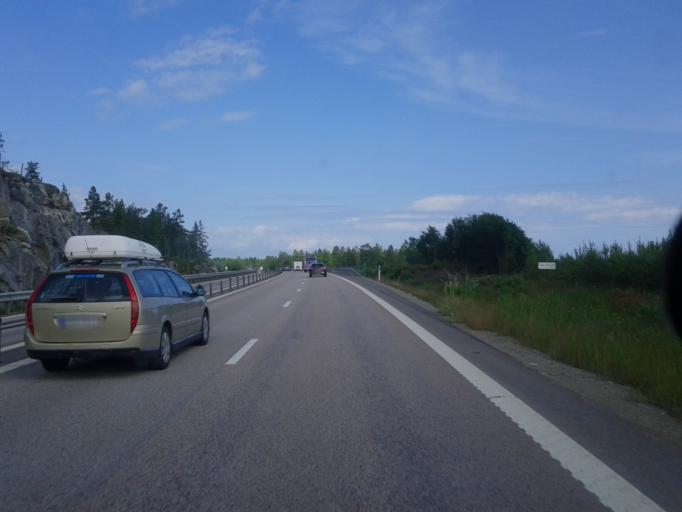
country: SE
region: Vaesternorrland
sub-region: OErnskoeldsviks Kommun
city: Husum
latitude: 63.3668
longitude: 19.1854
